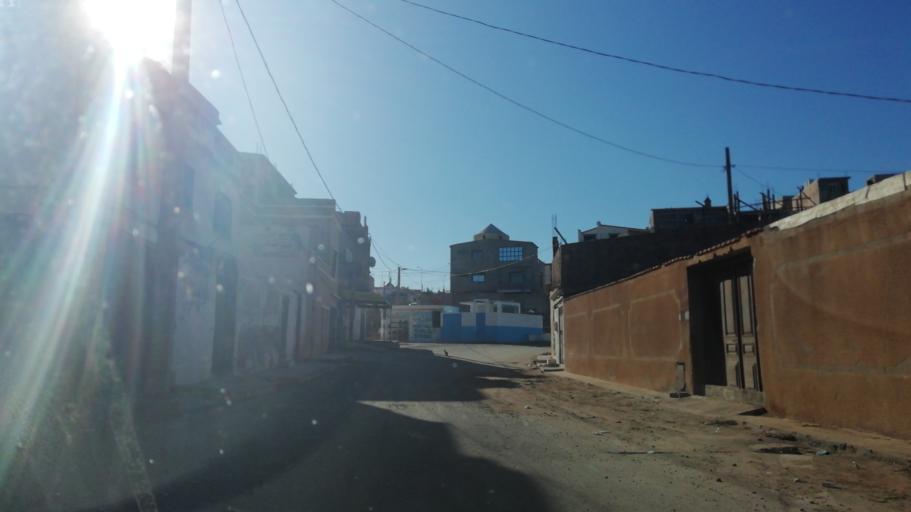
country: DZ
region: Oran
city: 'Ain el Turk
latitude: 35.7281
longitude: -0.8457
